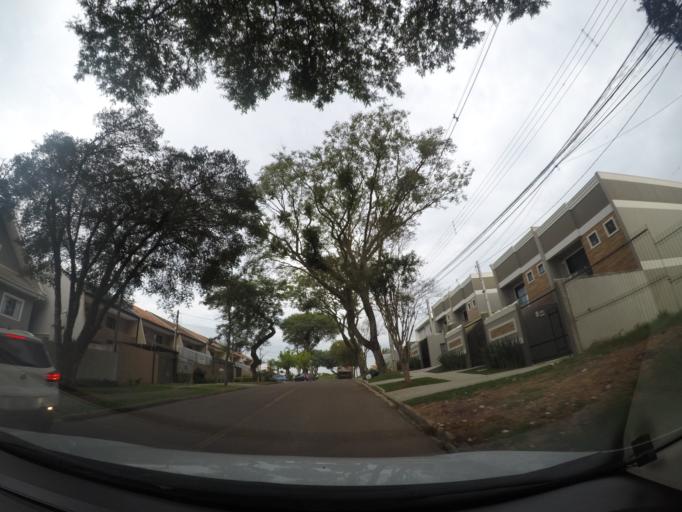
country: BR
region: Parana
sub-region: Sao Jose Dos Pinhais
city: Sao Jose dos Pinhais
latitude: -25.5139
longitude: -49.2383
